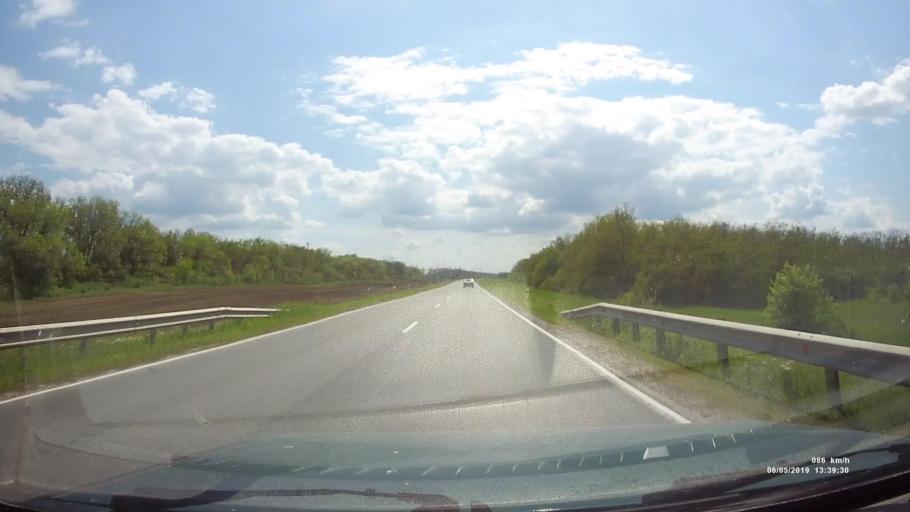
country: RU
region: Rostov
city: Ust'-Donetskiy
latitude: 47.6749
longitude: 40.7025
